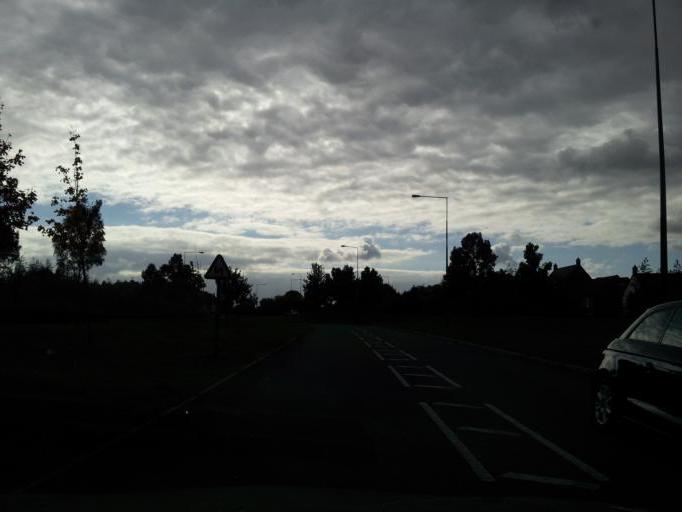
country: GB
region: England
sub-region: Milton Keynes
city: Shenley Church End
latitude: 52.0033
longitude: -0.8062
